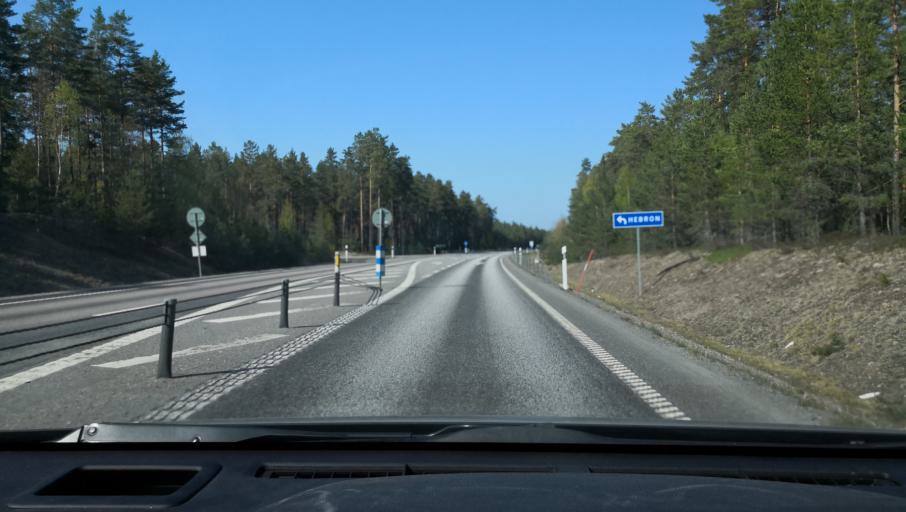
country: SE
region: Uppsala
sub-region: Heby Kommun
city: Tarnsjo
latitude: 60.1903
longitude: 16.9451
